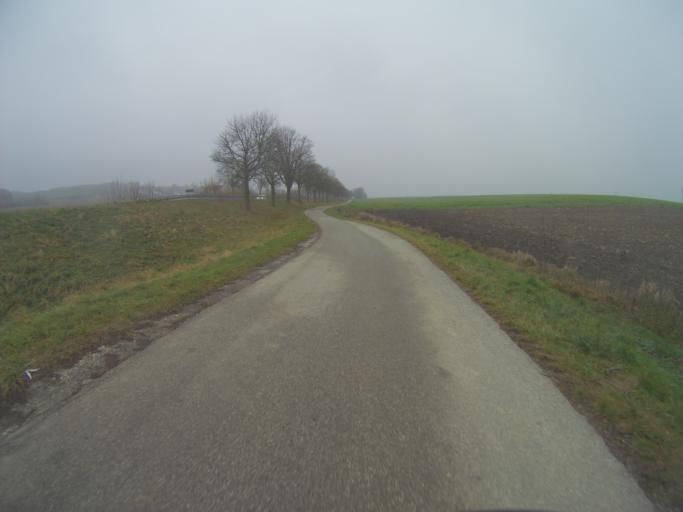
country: DE
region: Bavaria
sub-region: Upper Bavaria
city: Langenbach
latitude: 48.4312
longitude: 11.8355
